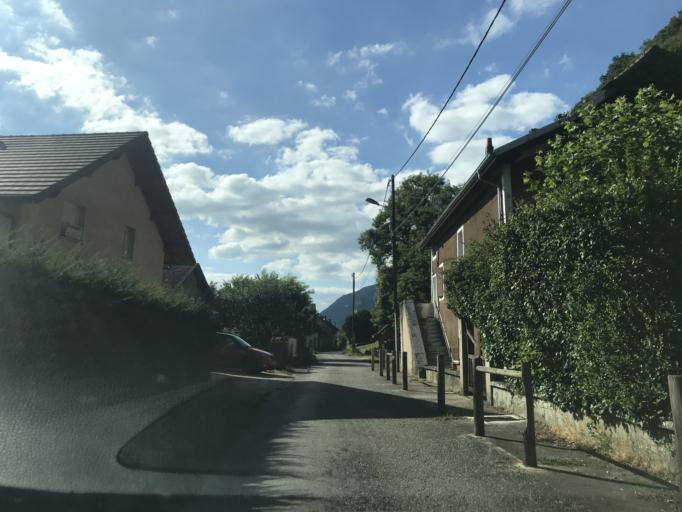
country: FR
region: Rhone-Alpes
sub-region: Departement de l'Ain
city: Culoz
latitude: 45.8268
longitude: 5.8031
